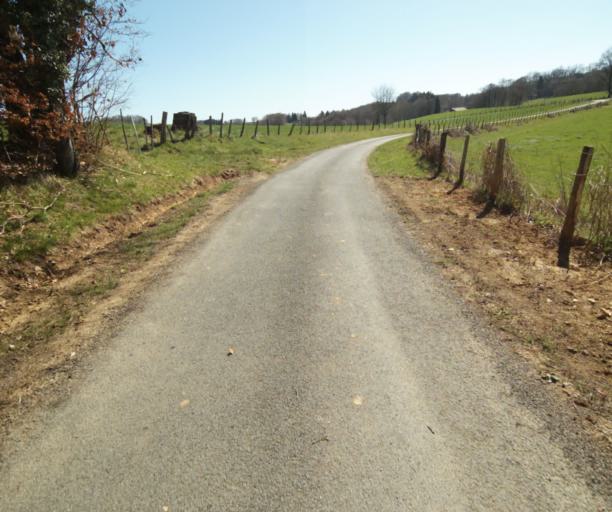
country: FR
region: Limousin
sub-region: Departement de la Correze
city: Uzerche
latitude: 45.3965
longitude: 1.6090
